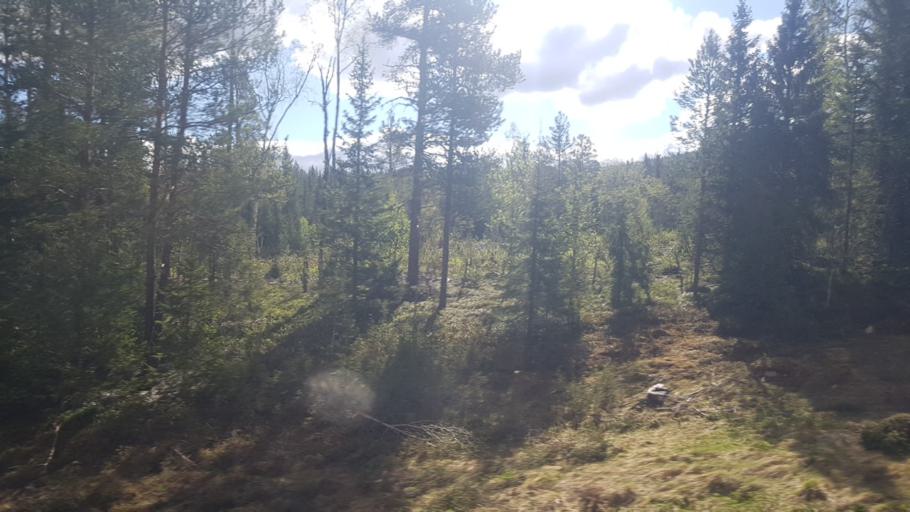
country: NO
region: Sor-Trondelag
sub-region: Rennebu
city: Berkak
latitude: 62.9045
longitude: 10.1202
